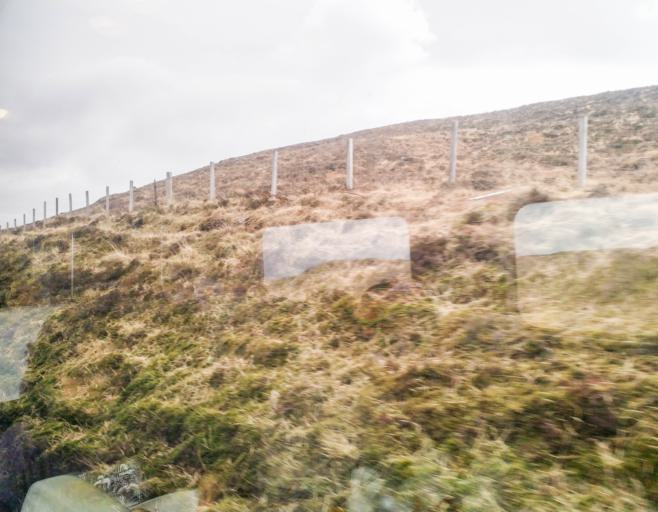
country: GB
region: Scotland
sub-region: Highland
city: Spean Bridge
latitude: 56.5937
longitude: -4.6371
